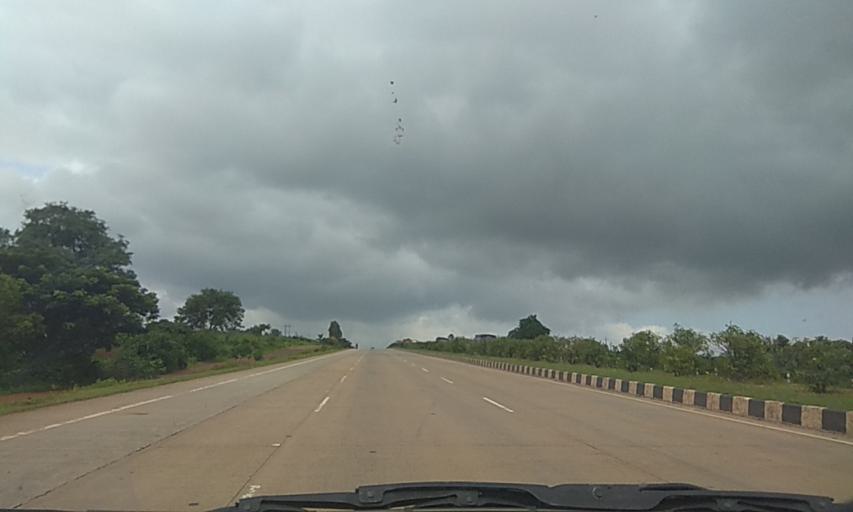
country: IN
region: Karnataka
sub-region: Dharwad
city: Alnavar
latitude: 15.5495
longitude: 74.8588
